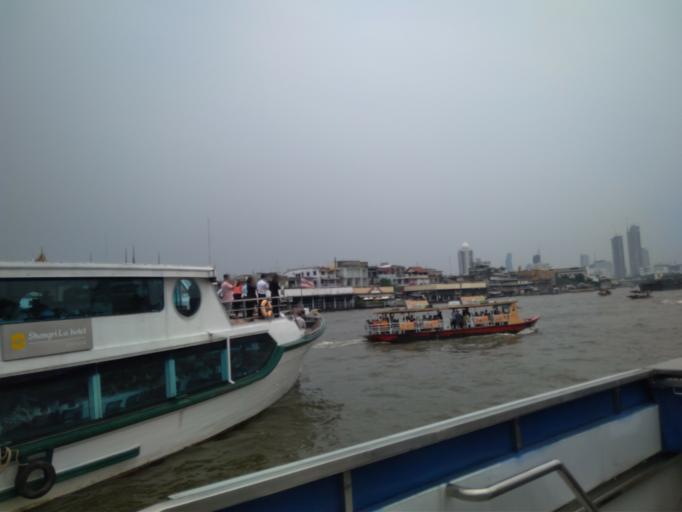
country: TH
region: Bangkok
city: Bangkok
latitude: 13.7457
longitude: 100.4889
